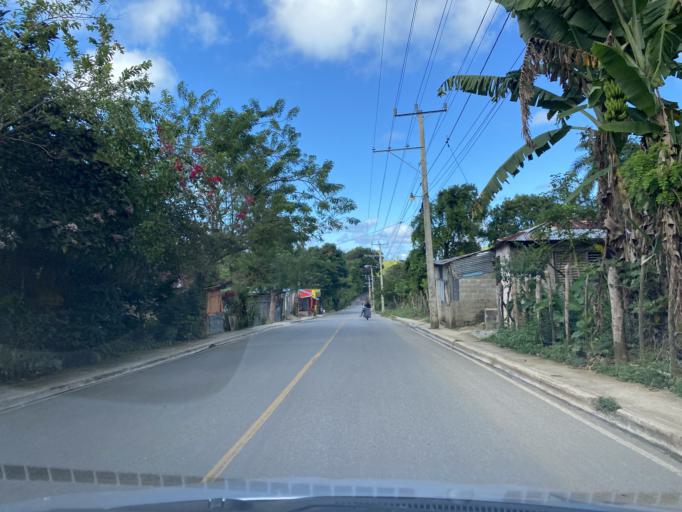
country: DO
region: Samana
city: Las Terrenas
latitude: 19.2887
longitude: -69.5480
